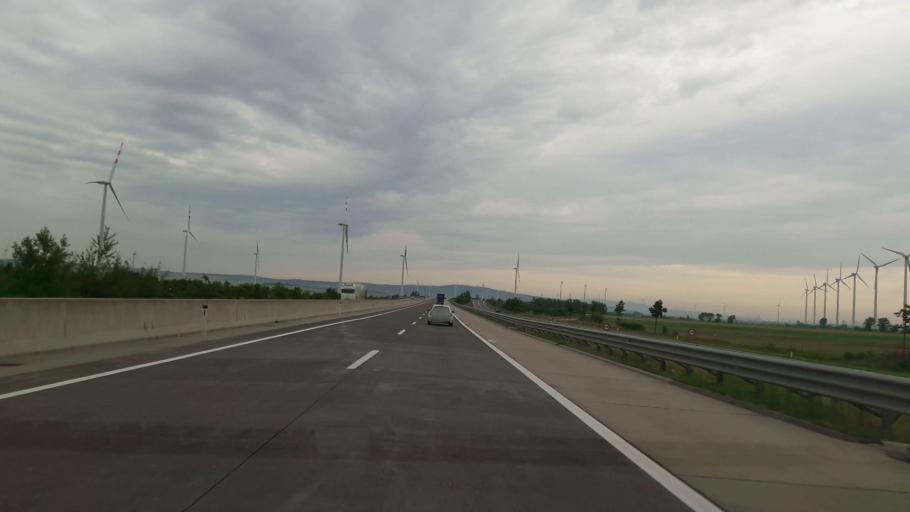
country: AT
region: Burgenland
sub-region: Politischer Bezirk Neusiedl am See
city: Gattendorf
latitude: 48.0447
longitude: 16.9932
